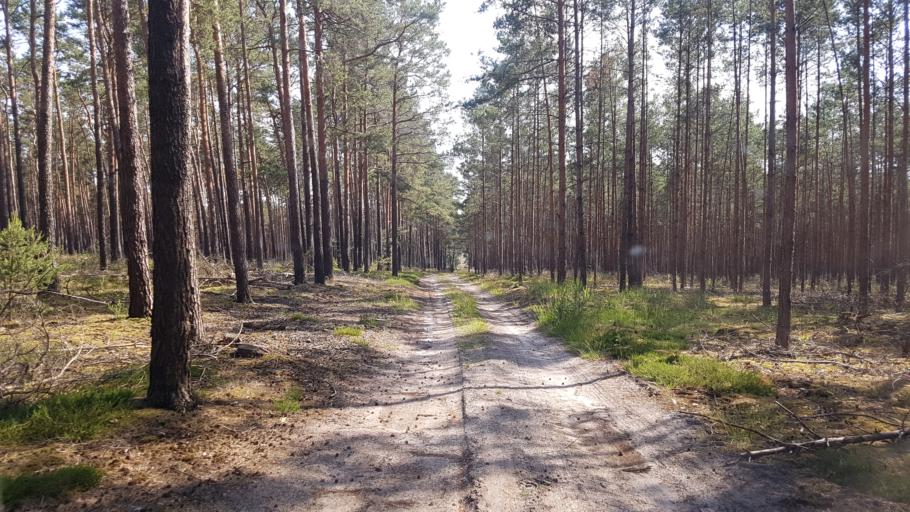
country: DE
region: Brandenburg
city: Trobitz
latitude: 51.6413
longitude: 13.4317
